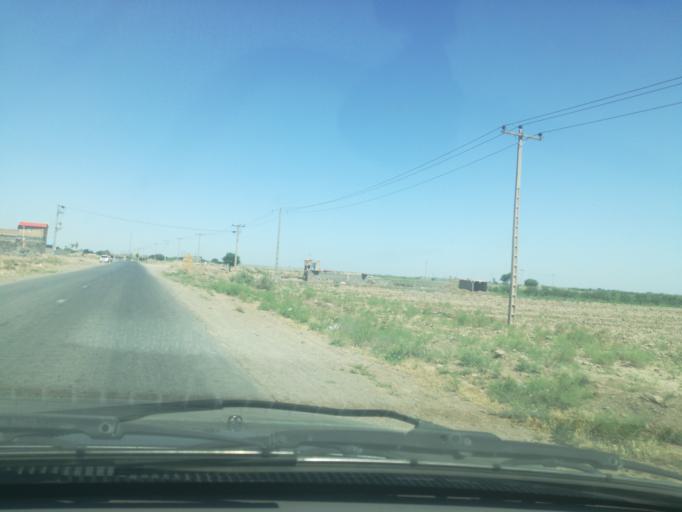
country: IR
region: Razavi Khorasan
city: Sarakhs
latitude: 36.5656
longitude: 61.1425
